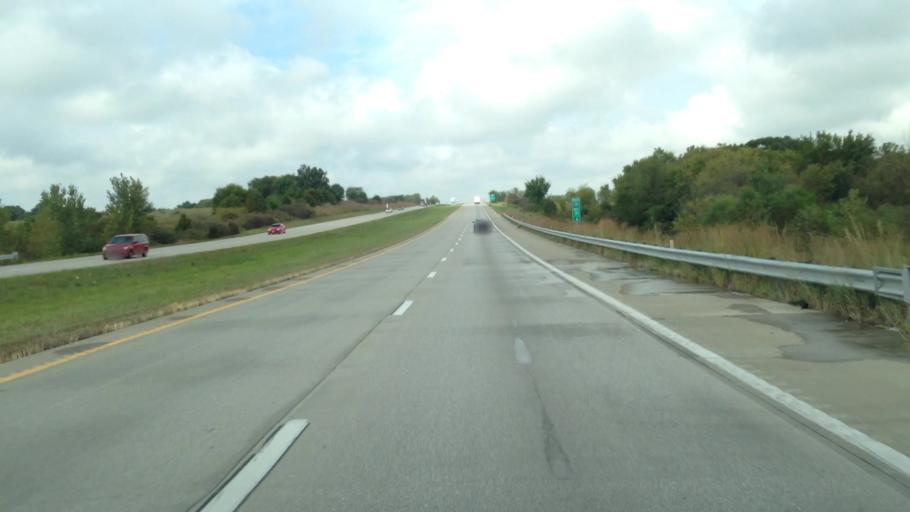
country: US
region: Missouri
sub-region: Clay County
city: Kearney
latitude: 39.4399
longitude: -94.3326
